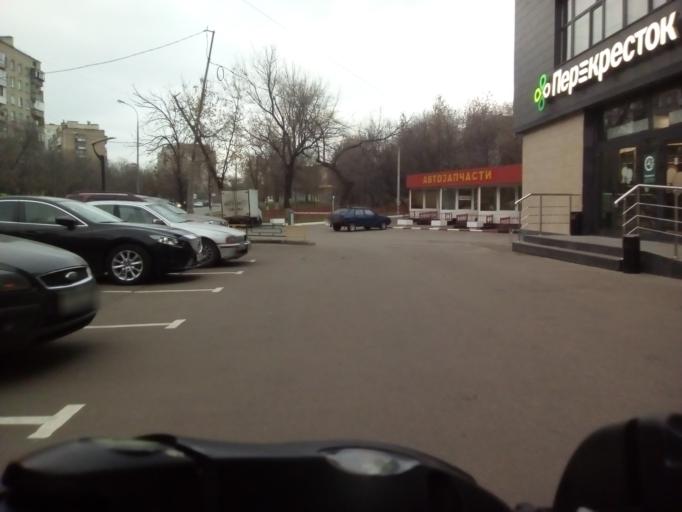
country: RU
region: Moscow
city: Lefortovo
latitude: 55.7618
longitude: 37.7178
